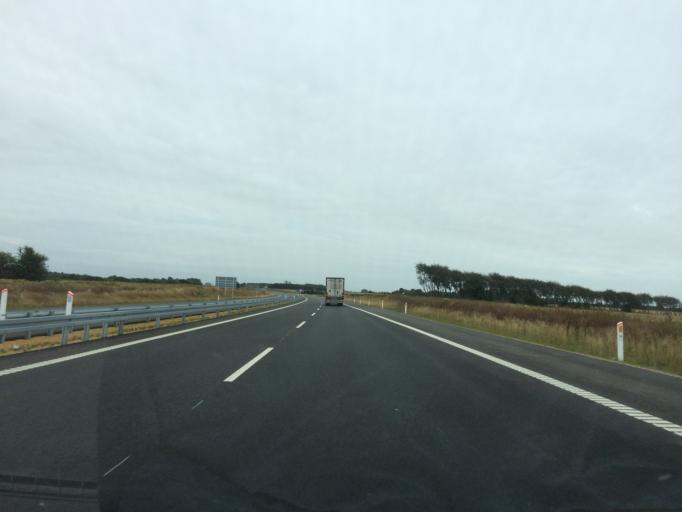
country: DK
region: Central Jutland
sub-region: Herning Kommune
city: Snejbjerg
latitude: 56.1465
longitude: 8.8702
